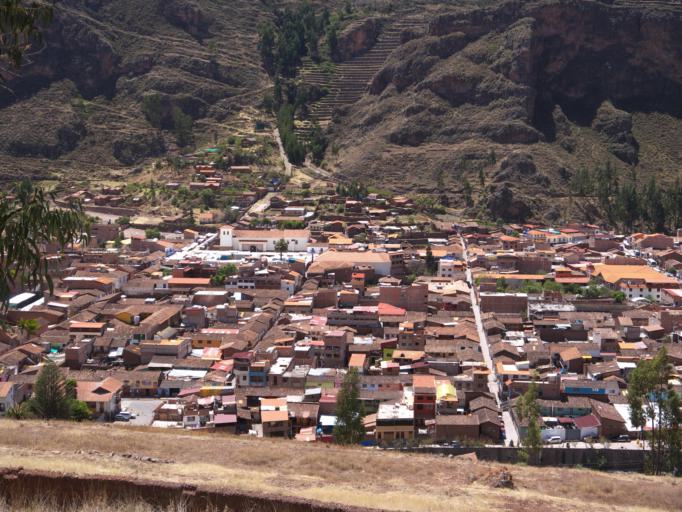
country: PE
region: Cusco
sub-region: Provincia de Calca
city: Pisac
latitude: -13.4256
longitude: -71.8511
